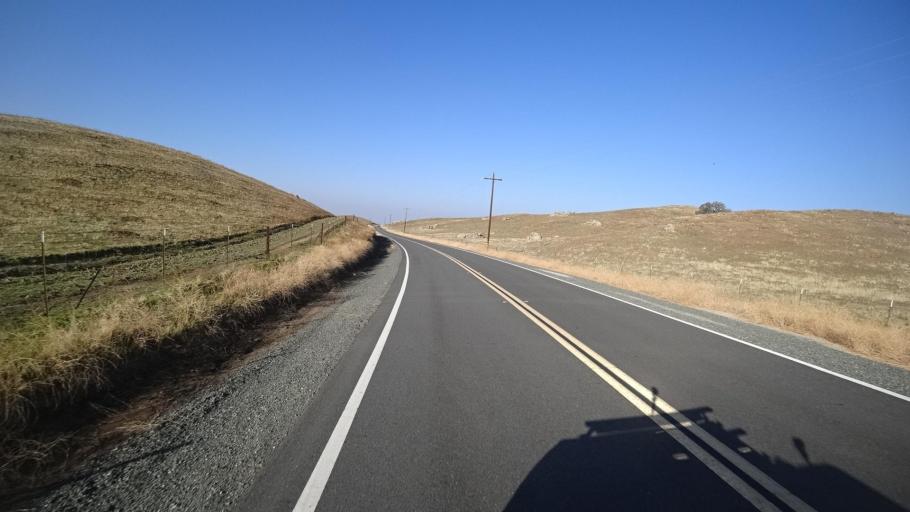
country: US
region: California
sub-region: Tulare County
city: Richgrove
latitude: 35.7422
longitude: -118.8885
